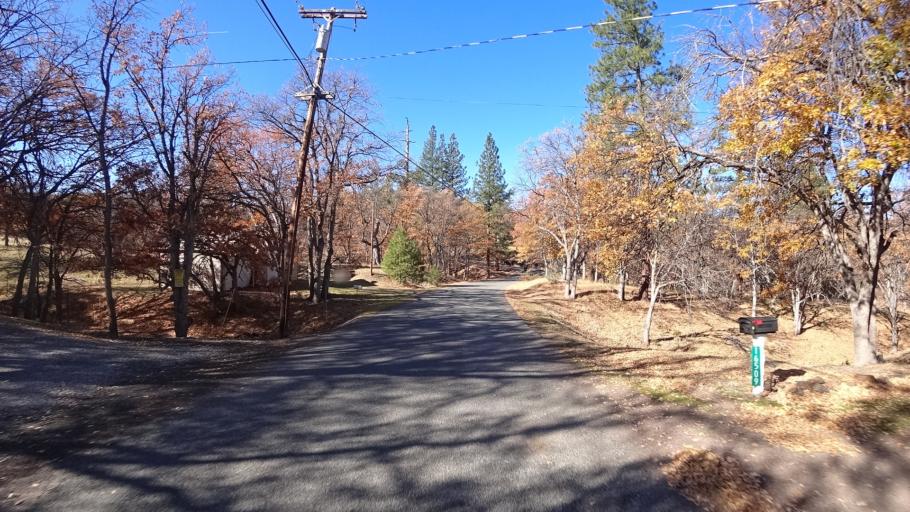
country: US
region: California
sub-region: Siskiyou County
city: Montague
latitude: 41.9738
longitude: -122.3202
